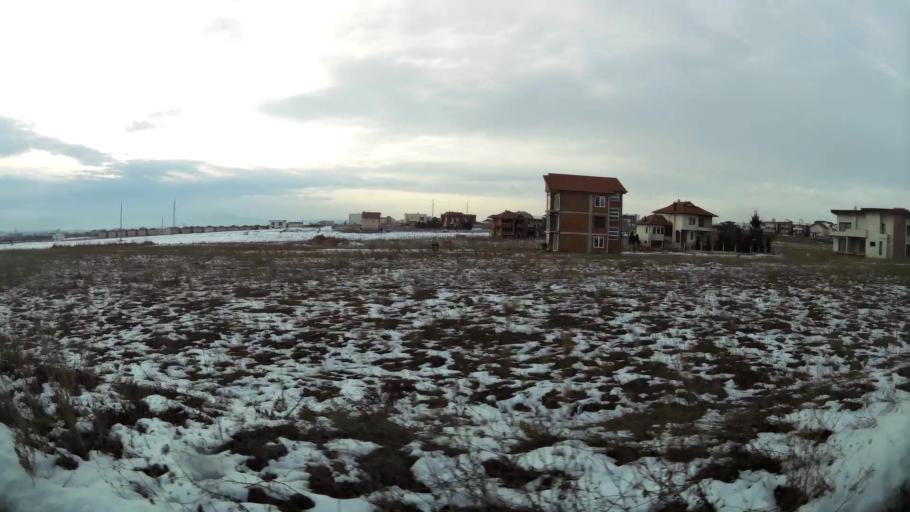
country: XK
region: Pristina
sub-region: Komuna e Prishtines
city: Pristina
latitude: 42.6239
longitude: 21.1588
